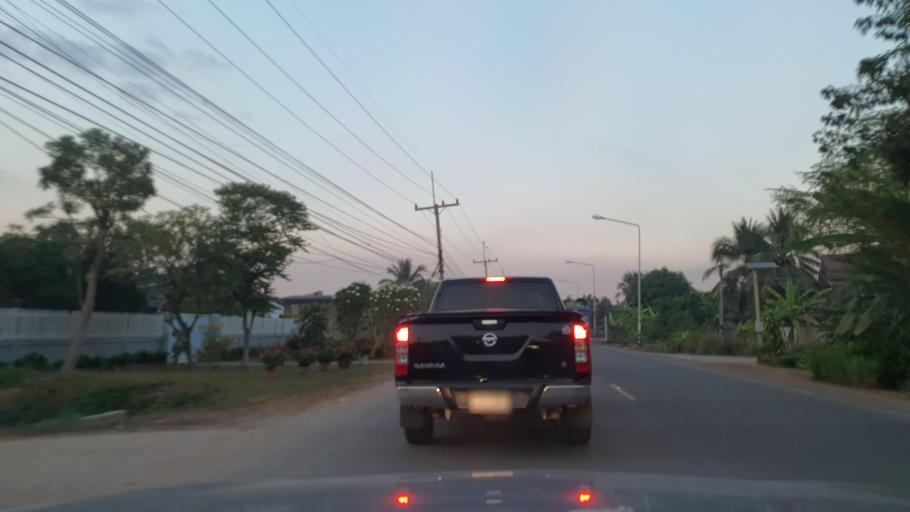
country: TH
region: Phayao
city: Dok Kham Tai
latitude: 19.0835
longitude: 100.0631
